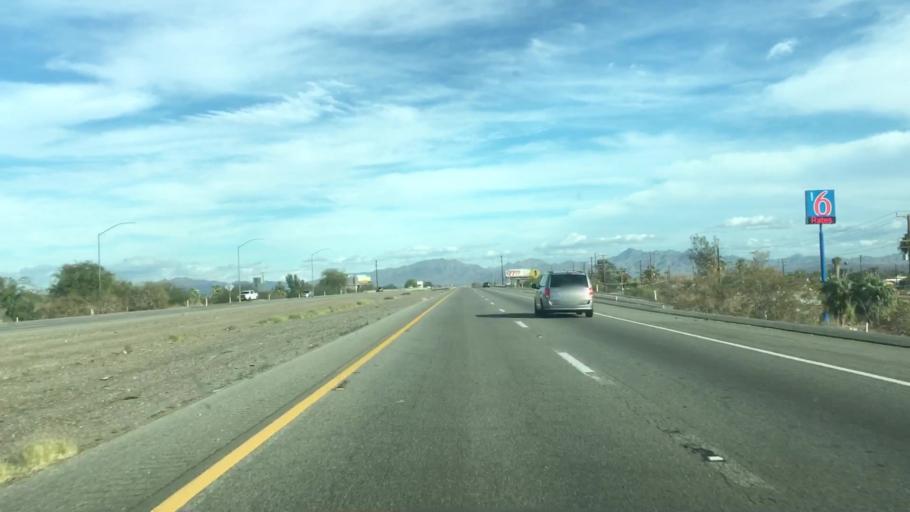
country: US
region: California
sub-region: Riverside County
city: Blythe
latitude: 33.6070
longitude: -114.6038
